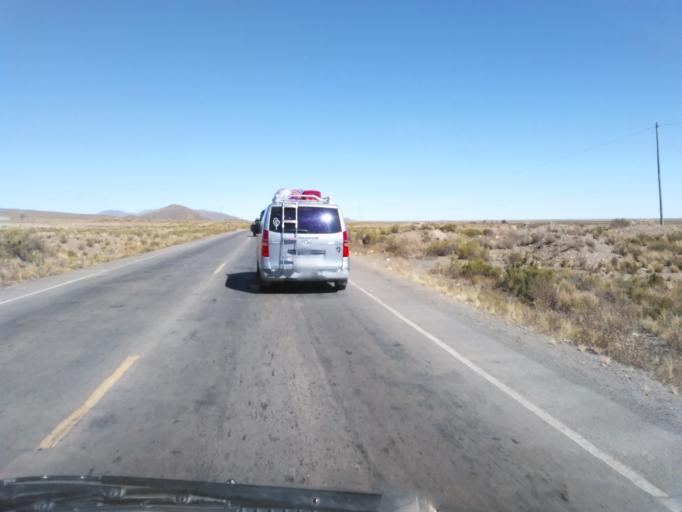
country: BO
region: Oruro
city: Machacamarca
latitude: -18.0723
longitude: -67.0057
